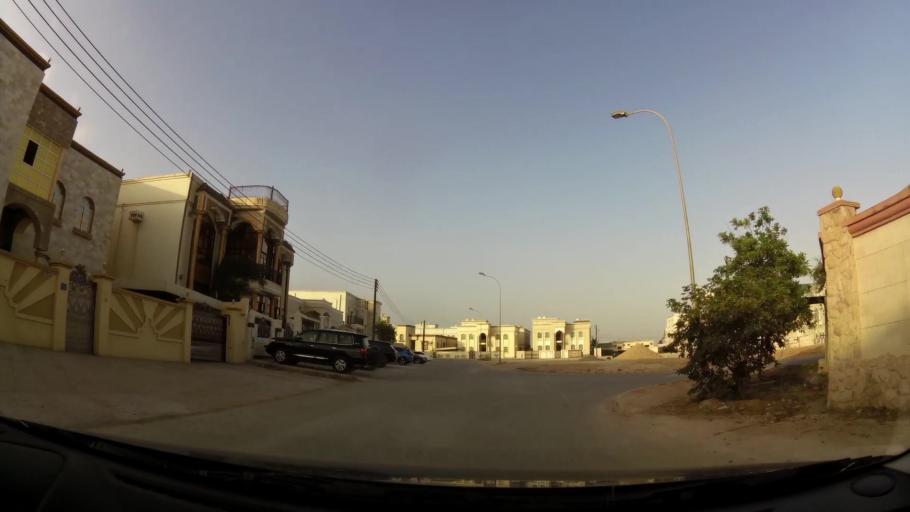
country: OM
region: Zufar
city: Salalah
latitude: 17.0182
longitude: 54.0328
